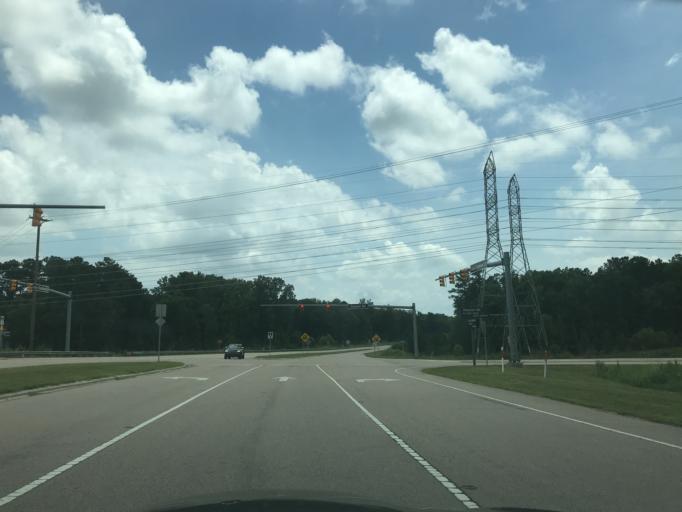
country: US
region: North Carolina
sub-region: Wake County
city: Morrisville
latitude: 35.8754
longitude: -78.8830
